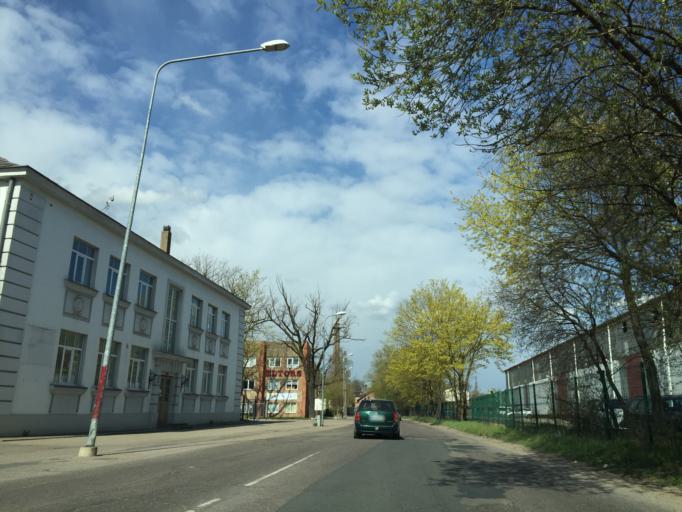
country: LV
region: Riga
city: Riga
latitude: 56.9287
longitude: 24.1019
